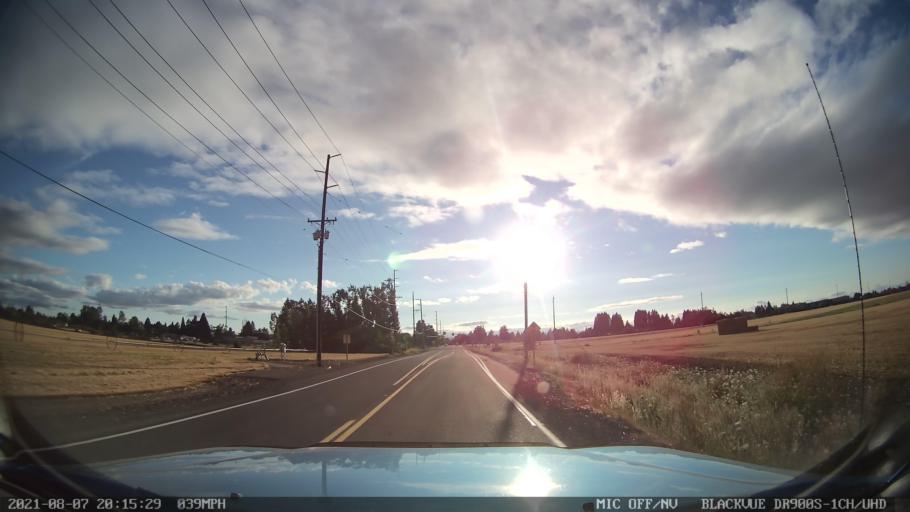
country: US
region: Oregon
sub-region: Marion County
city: Four Corners
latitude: 44.9549
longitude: -122.9564
